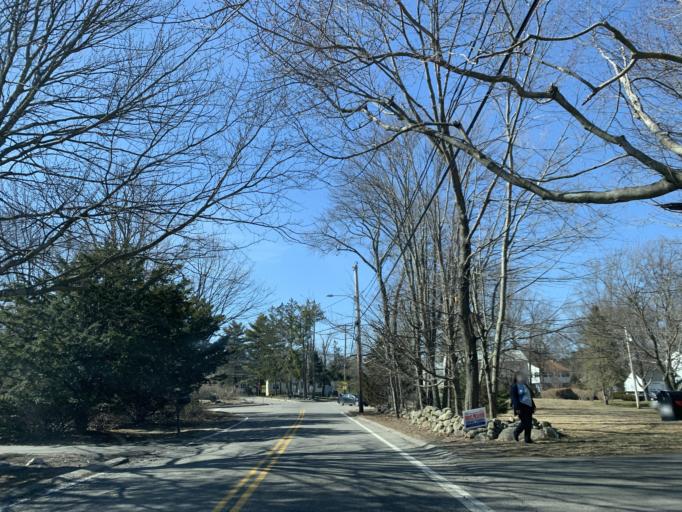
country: US
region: Massachusetts
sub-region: Norfolk County
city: Norwood
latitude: 42.1583
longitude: -71.1941
